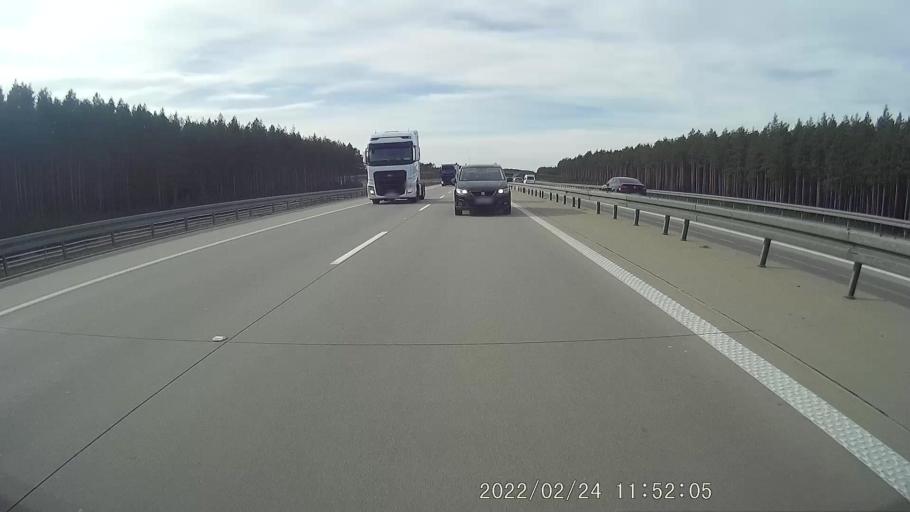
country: PL
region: Lower Silesian Voivodeship
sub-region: Powiat polkowicki
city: Radwanice
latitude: 51.6188
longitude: 15.9730
